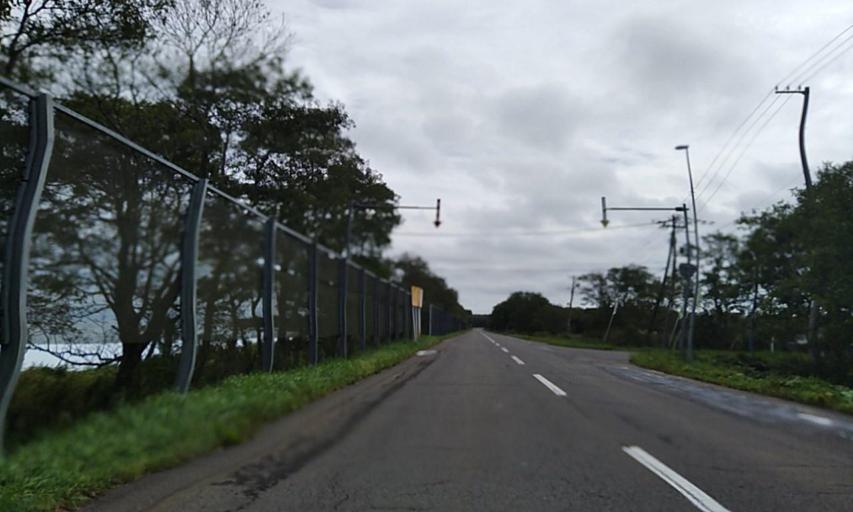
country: JP
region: Hokkaido
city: Shibetsu
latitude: 43.5928
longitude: 145.2037
